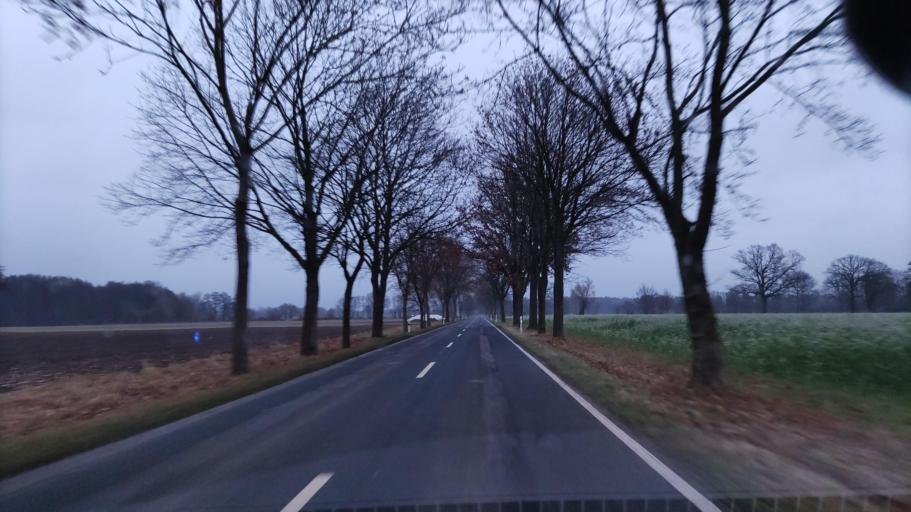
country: DE
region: Lower Saxony
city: Waddeweitz
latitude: 53.0263
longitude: 11.0132
